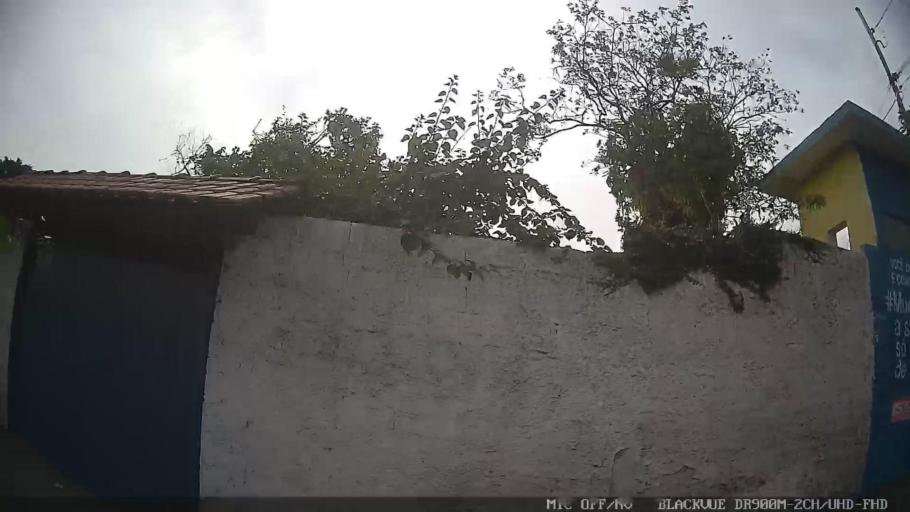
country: BR
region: Sao Paulo
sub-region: Itaquaquecetuba
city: Itaquaquecetuba
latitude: -23.4979
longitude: -46.3488
